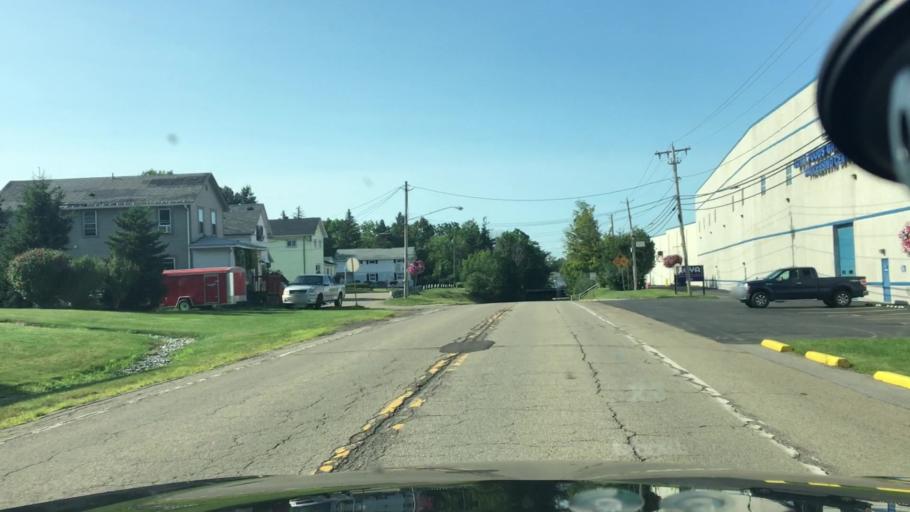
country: US
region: New York
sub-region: Erie County
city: Angola
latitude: 42.6295
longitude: -79.0273
